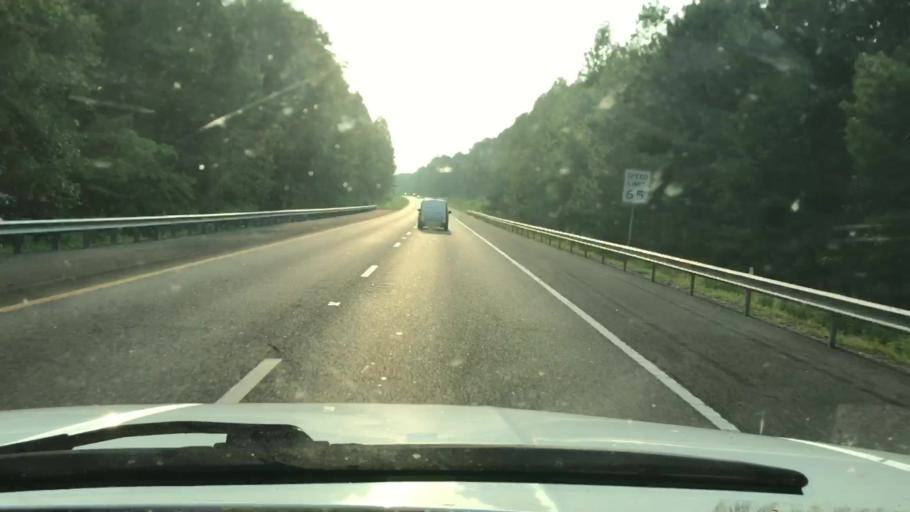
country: US
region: Virginia
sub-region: Chesterfield County
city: Brandermill
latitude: 37.4112
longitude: -77.5813
